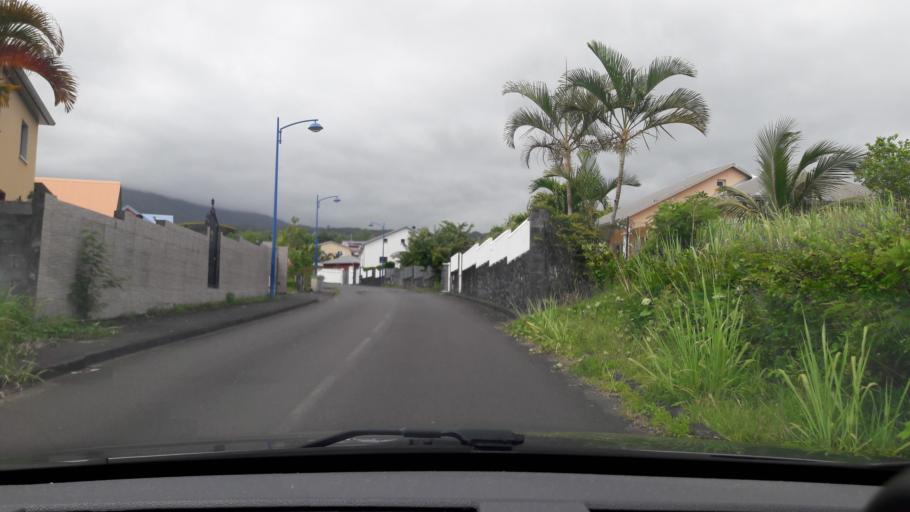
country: RE
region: Reunion
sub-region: Reunion
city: Saint-Benoit
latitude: -21.0929
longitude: 55.7038
